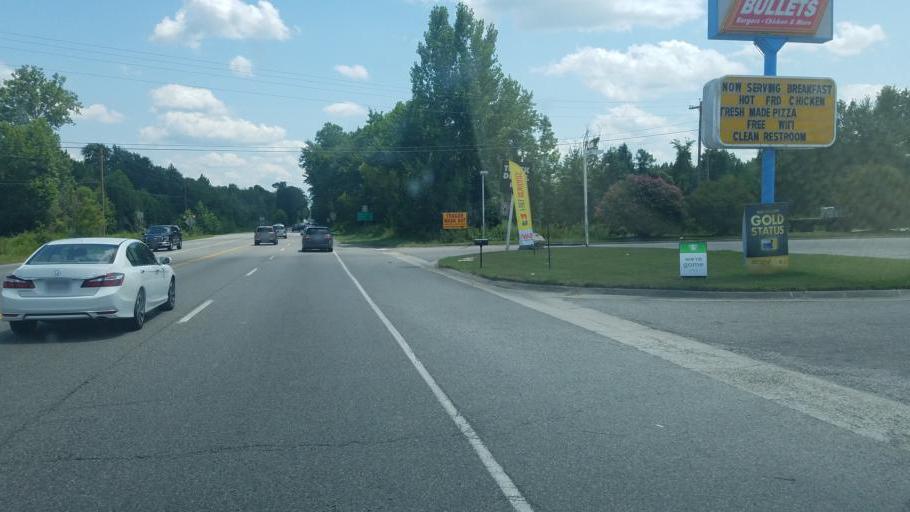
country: US
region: Virginia
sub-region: Prince George County
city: Prince George
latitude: 37.1553
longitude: -77.2745
